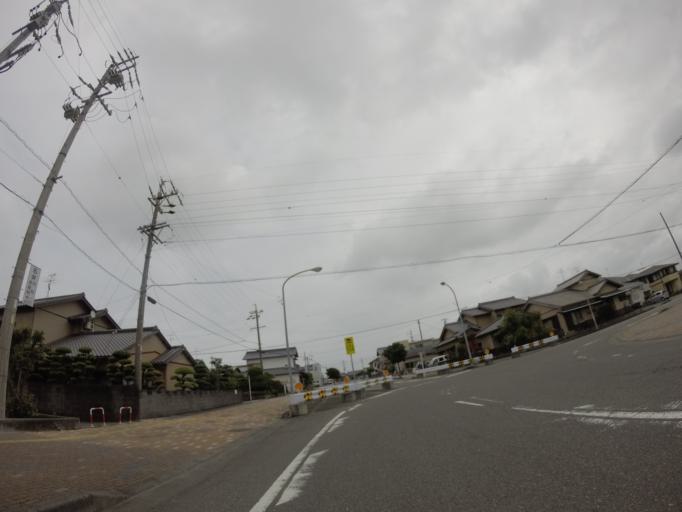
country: JP
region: Shizuoka
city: Sagara
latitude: 34.7367
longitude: 138.2234
